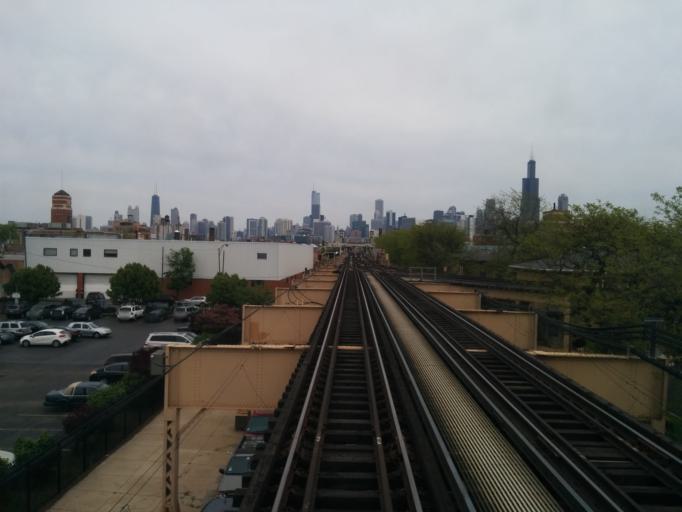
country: US
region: Illinois
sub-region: Cook County
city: Chicago
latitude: 41.8853
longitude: -87.6703
